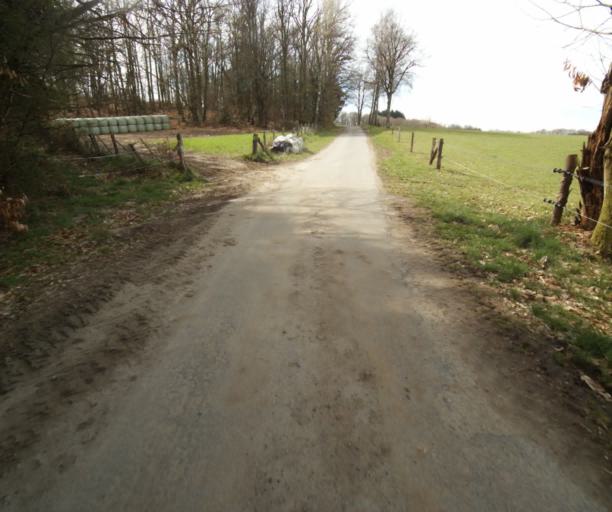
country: FR
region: Limousin
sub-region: Departement de la Correze
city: Correze
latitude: 45.3620
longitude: 1.9074
